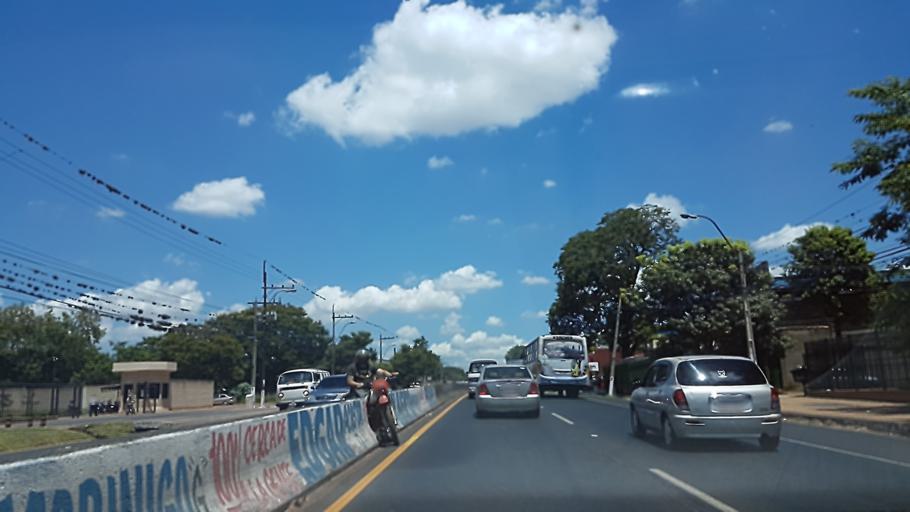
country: PY
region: Central
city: Capiata
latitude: -25.3477
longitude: -57.4665
